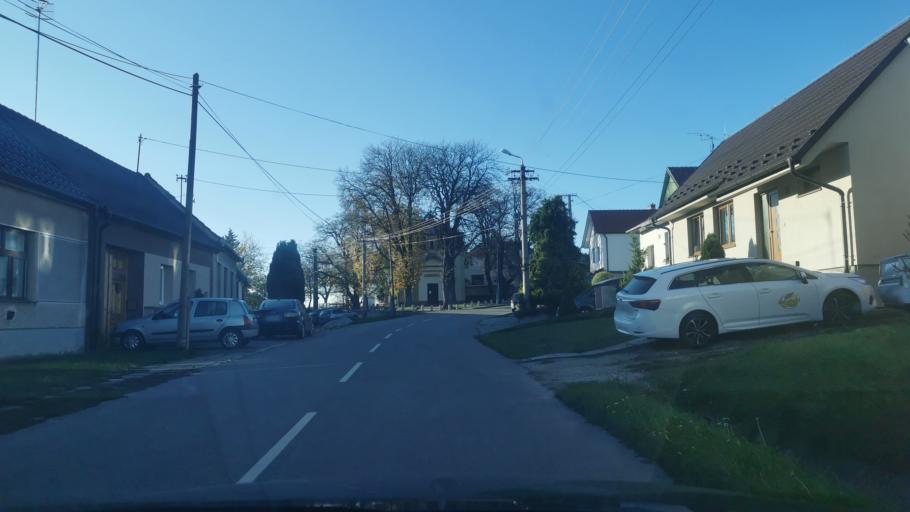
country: SK
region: Trnavsky
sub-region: Okres Skalica
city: Skalica
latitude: 48.7739
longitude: 17.2730
